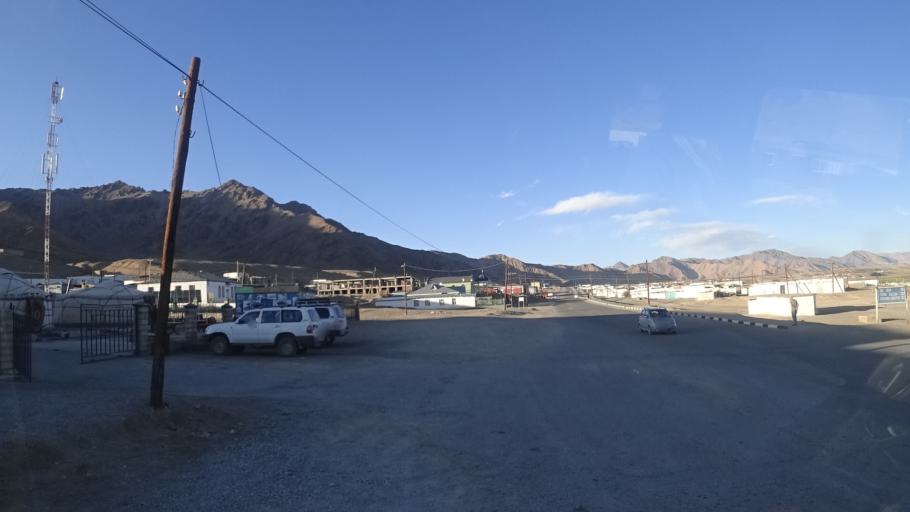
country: TJ
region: Gorno-Badakhshan
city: Murghob
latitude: 38.1741
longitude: 73.9670
